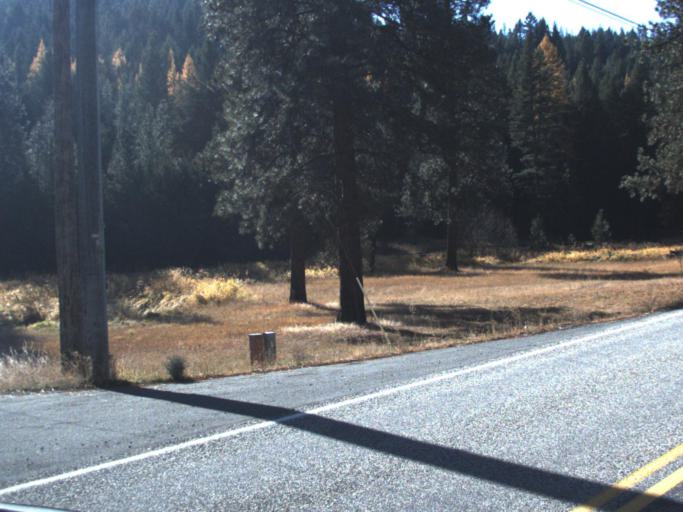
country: US
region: Washington
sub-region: Ferry County
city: Republic
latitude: 48.7800
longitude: -118.6301
